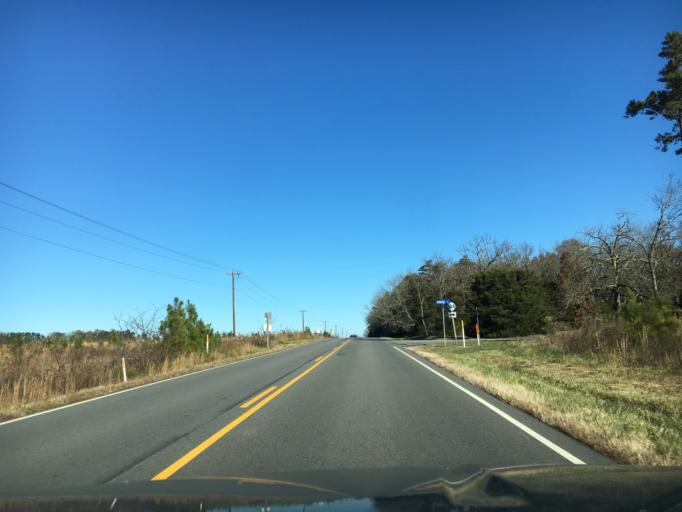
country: US
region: Virginia
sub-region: Buckingham County
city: Buckingham
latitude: 37.5281
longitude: -78.6162
